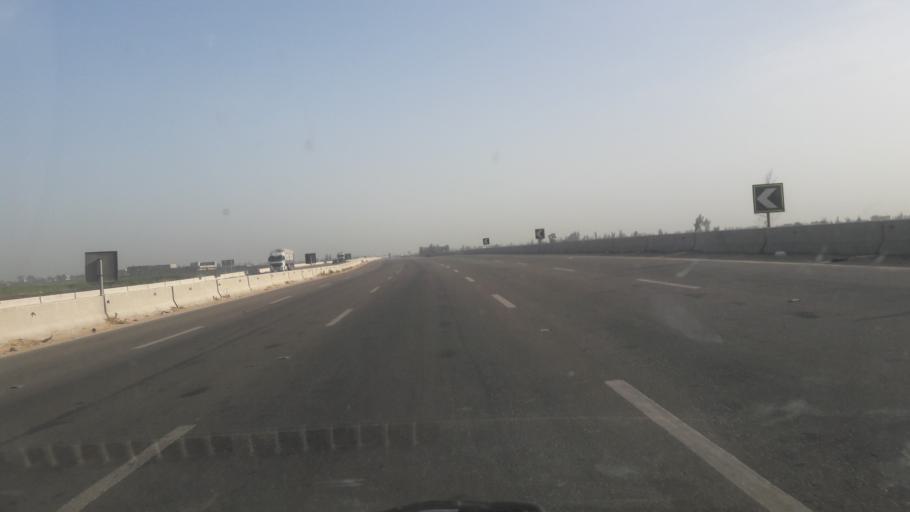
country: EG
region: Muhafazat Bur Sa`id
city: Port Said
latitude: 31.0240
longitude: 32.2365
